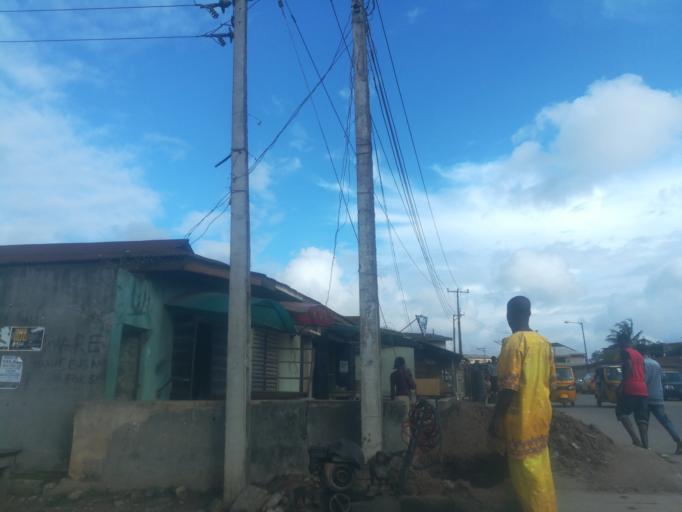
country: NG
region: Lagos
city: Somolu
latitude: 6.5403
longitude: 3.3812
